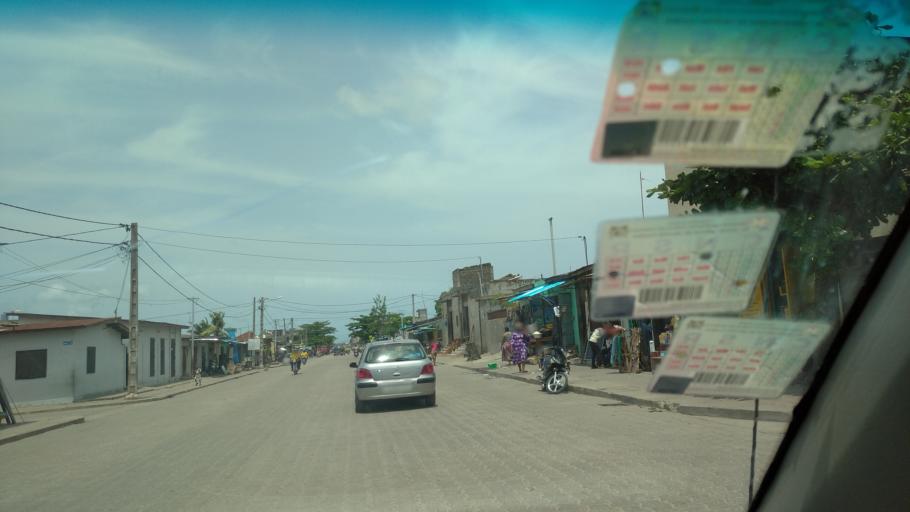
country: BJ
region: Littoral
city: Cotonou
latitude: 6.3906
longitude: 2.4589
